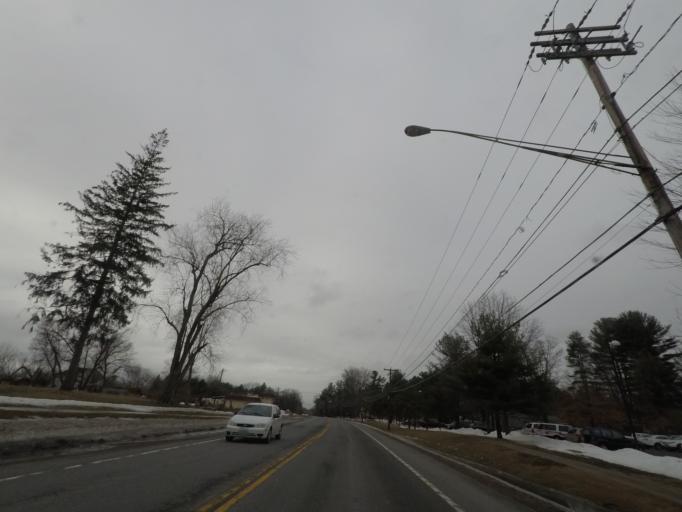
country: US
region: New York
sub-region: Albany County
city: Voorheesville
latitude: 42.7168
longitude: -73.9365
